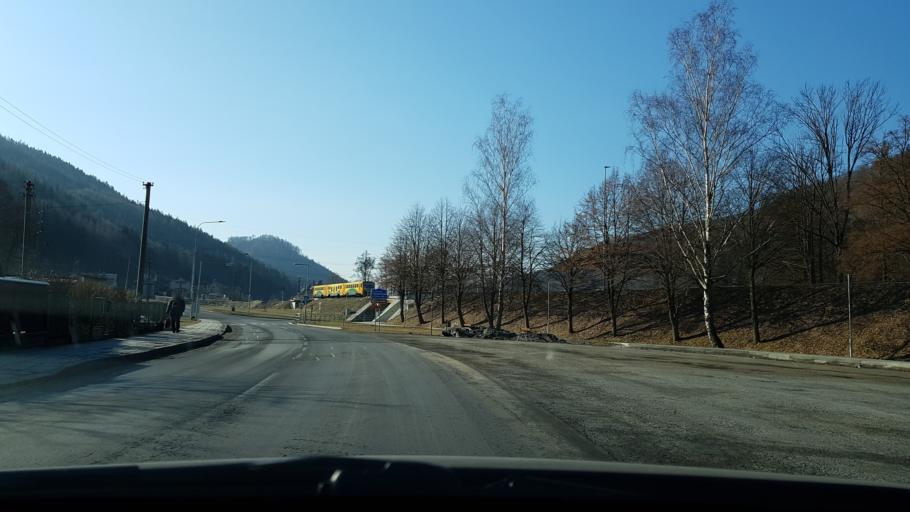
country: CZ
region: Olomoucky
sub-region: Okres Sumperk
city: Hanusovice
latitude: 50.0697
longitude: 16.9305
